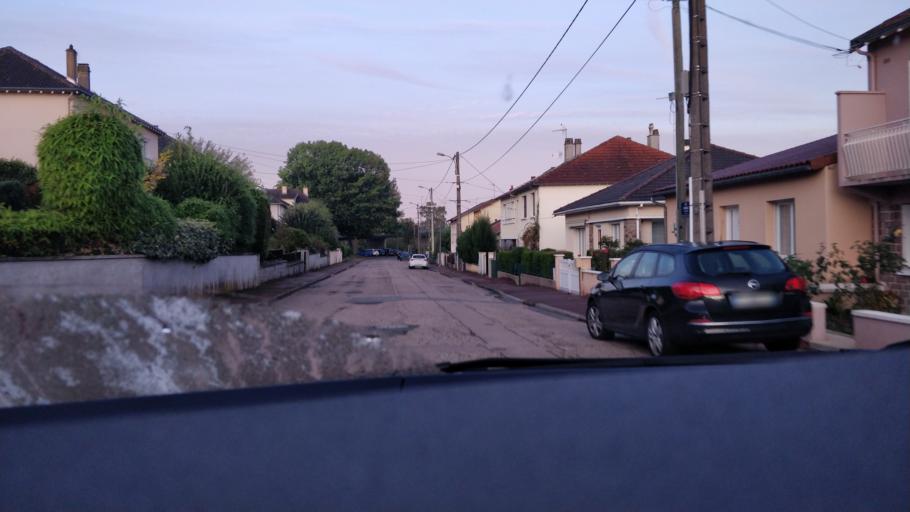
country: FR
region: Limousin
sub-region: Departement de la Haute-Vienne
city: Limoges
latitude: 45.8400
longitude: 1.2386
